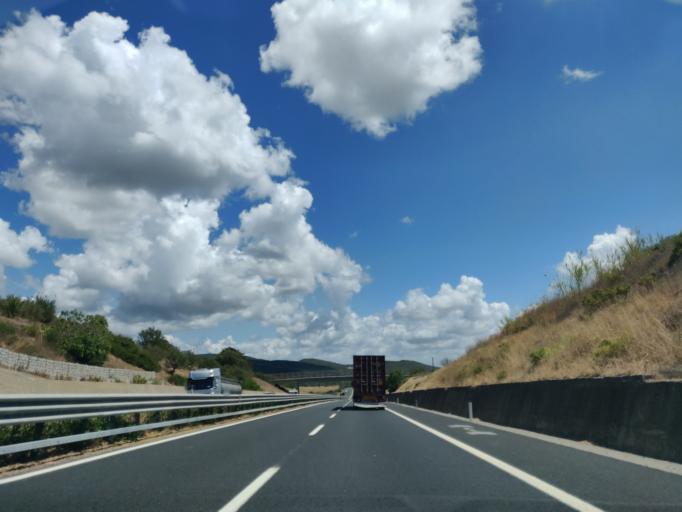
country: IT
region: Latium
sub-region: Citta metropolitana di Roma Capitale
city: Santa Marinella
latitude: 42.0432
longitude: 11.9102
